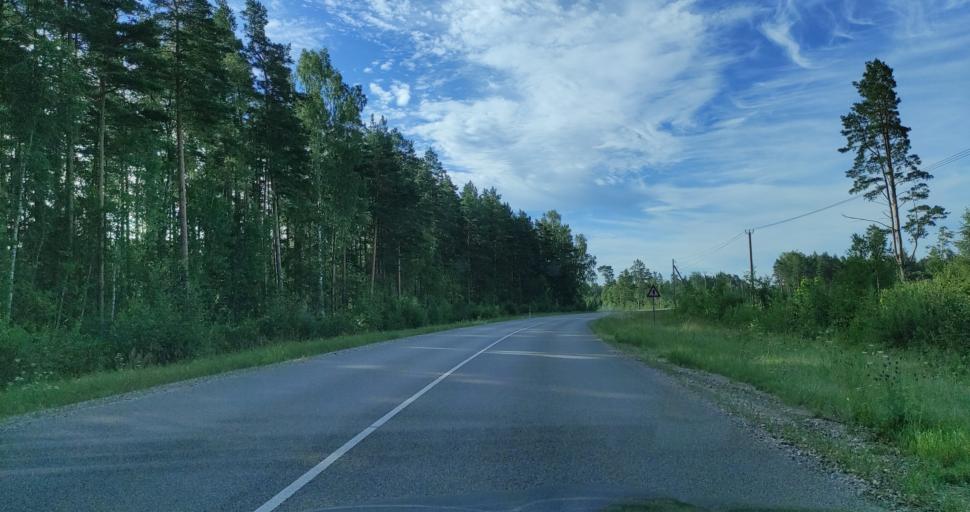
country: LV
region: Pavilostas
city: Pavilosta
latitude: 56.7903
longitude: 21.2460
